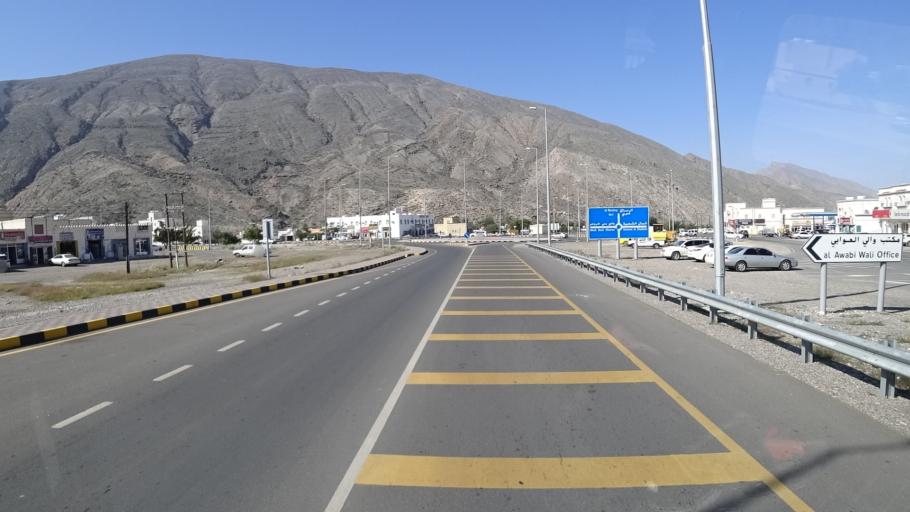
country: OM
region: Al Batinah
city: Bayt al `Awabi
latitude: 23.3114
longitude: 57.5217
